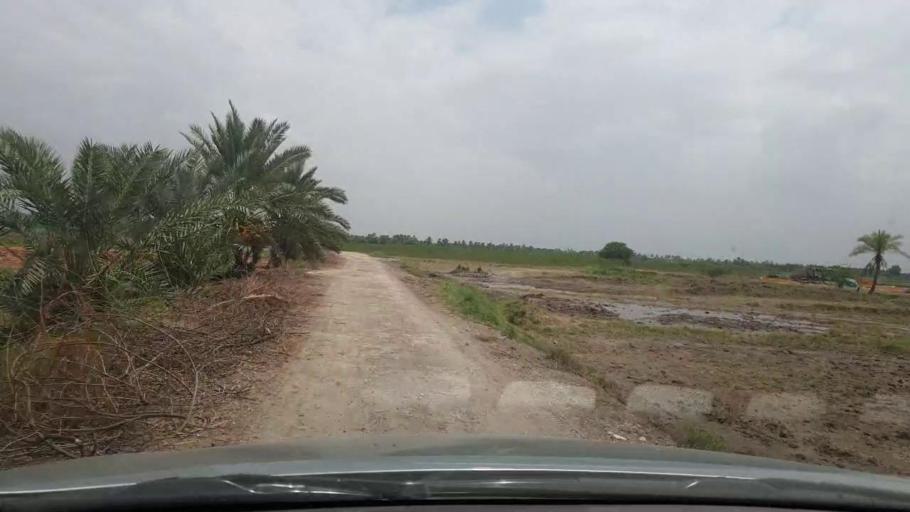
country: PK
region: Sindh
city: Kot Diji
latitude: 27.4280
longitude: 68.7589
